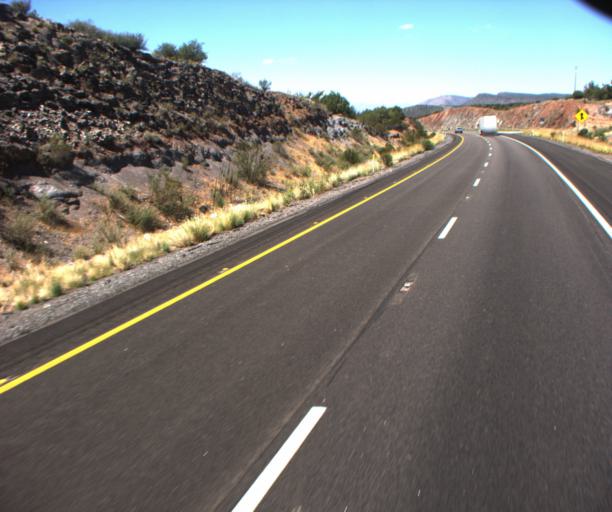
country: US
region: Arizona
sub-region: Mohave County
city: Peach Springs
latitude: 35.1911
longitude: -113.4368
